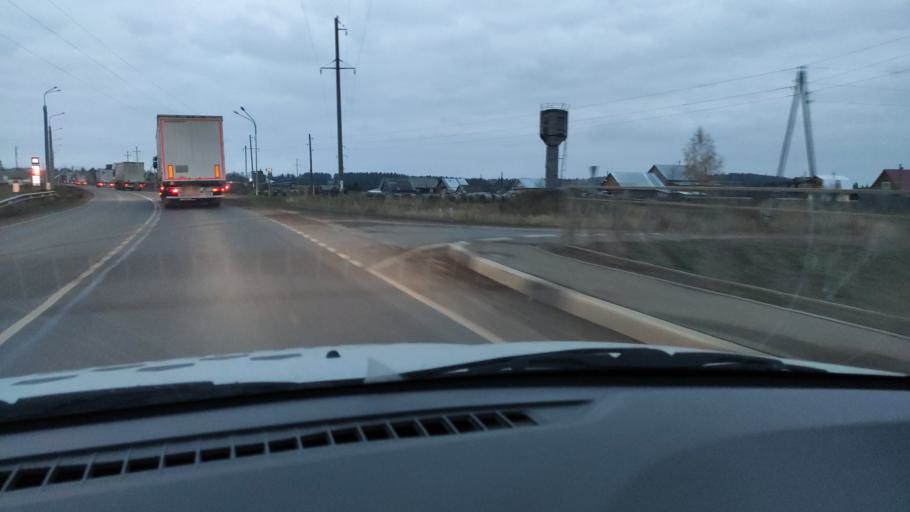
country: RU
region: Kirov
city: Kostino
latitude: 58.8514
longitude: 53.2673
